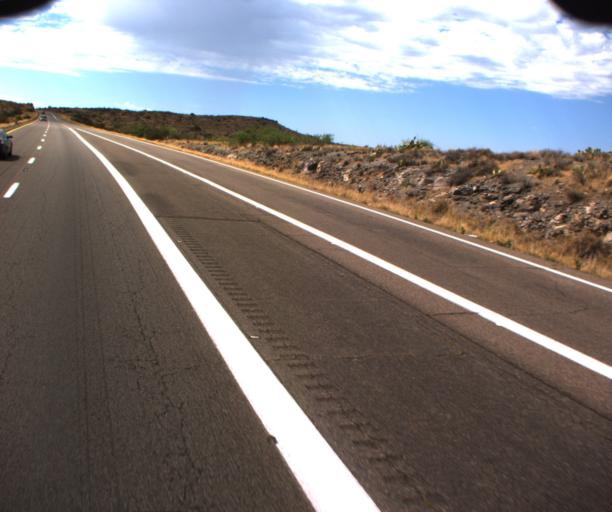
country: US
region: Arizona
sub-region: Yavapai County
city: Cordes Lakes
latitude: 34.2314
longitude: -112.1170
